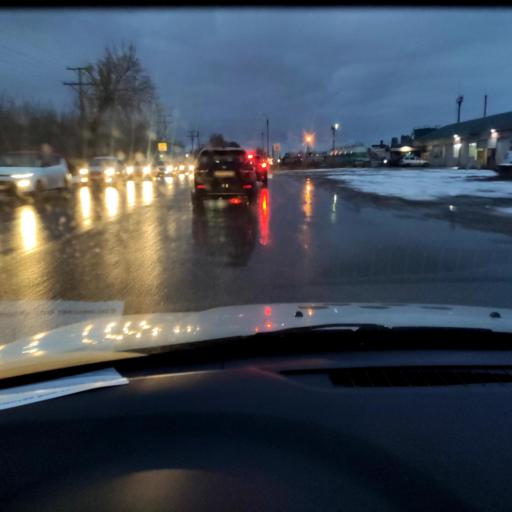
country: RU
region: Samara
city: Tol'yatti
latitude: 53.5311
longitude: 49.4613
